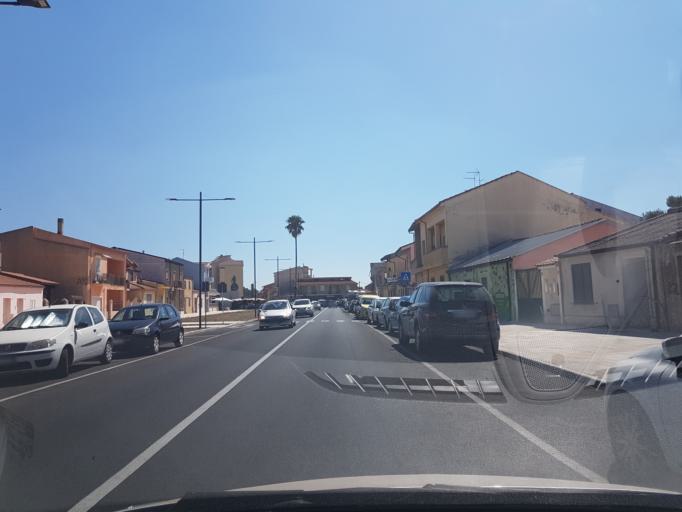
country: IT
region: Sardinia
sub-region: Provincia di Oristano
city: Oristano
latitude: 39.9002
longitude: 8.5999
